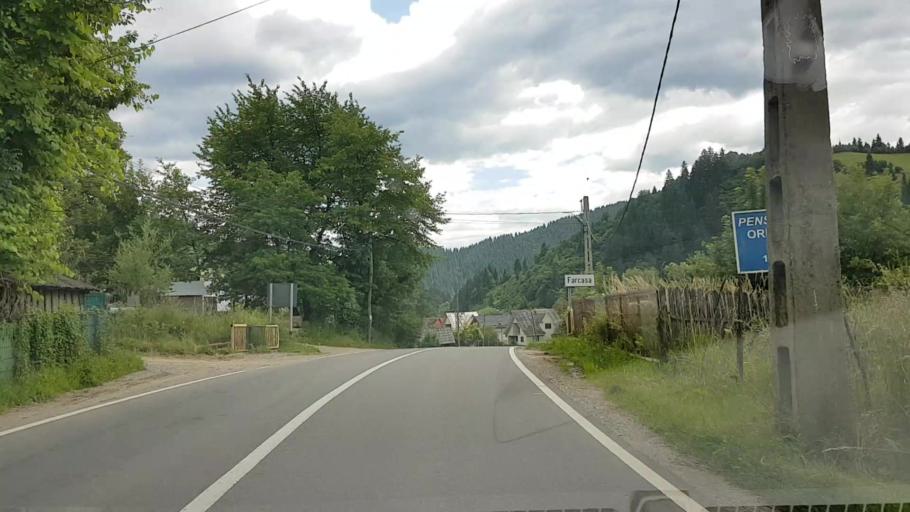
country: RO
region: Neamt
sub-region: Comuna Farcasa
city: Farcasa
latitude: 47.1587
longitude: 25.8309
